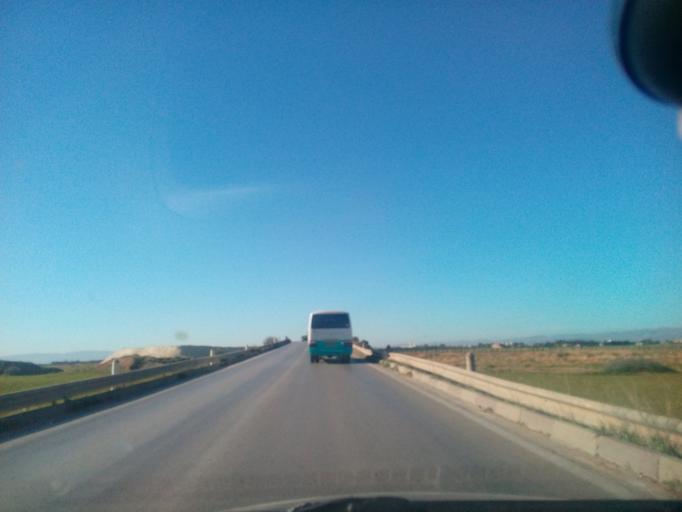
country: DZ
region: Relizane
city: Djidiouia
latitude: 35.8958
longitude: 0.7151
